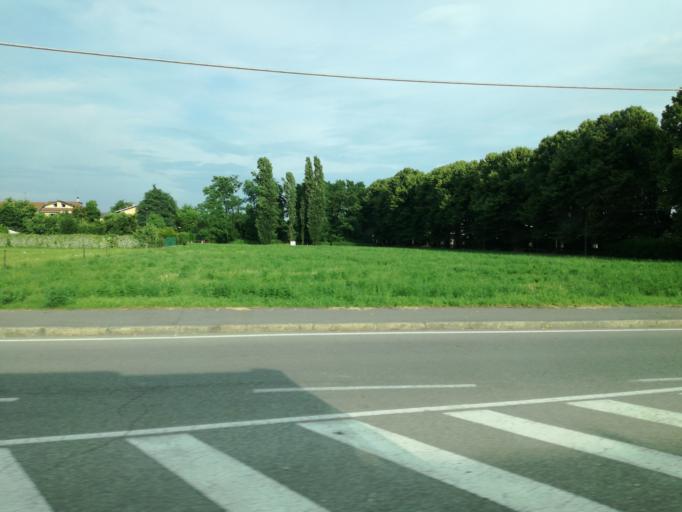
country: IT
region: Lombardy
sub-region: Provincia di Monza e Brianza
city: Arcore
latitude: 45.6247
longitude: 9.3261
